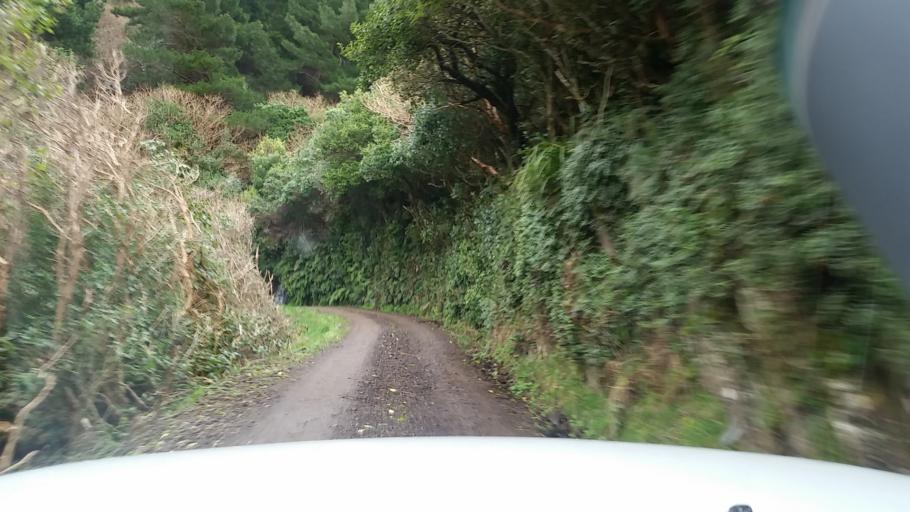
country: NZ
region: Canterbury
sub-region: Christchurch City
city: Christchurch
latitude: -43.7035
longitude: 172.7742
